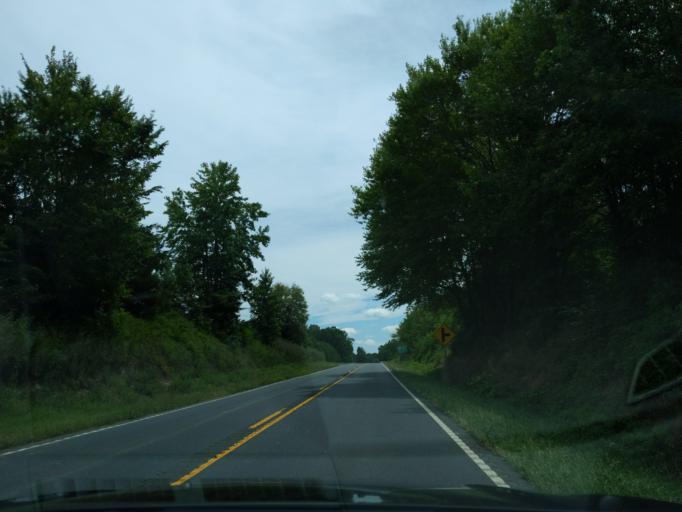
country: US
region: North Carolina
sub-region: Rowan County
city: Rockwell
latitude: 35.4588
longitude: -80.3248
